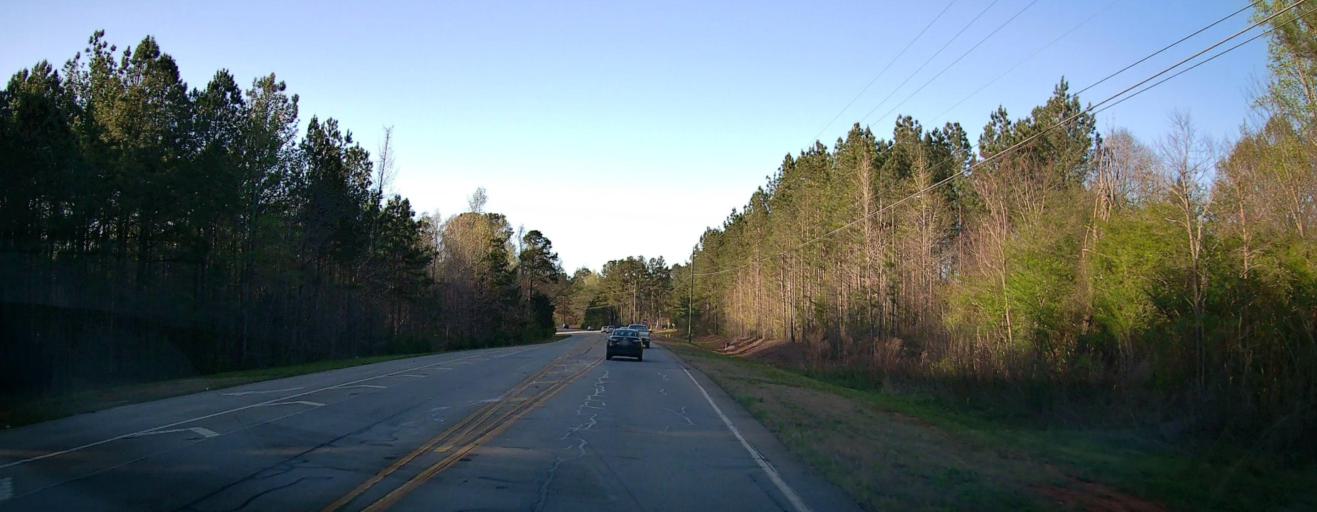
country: US
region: Georgia
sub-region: Newton County
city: Oakwood
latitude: 33.4538
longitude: -83.9035
